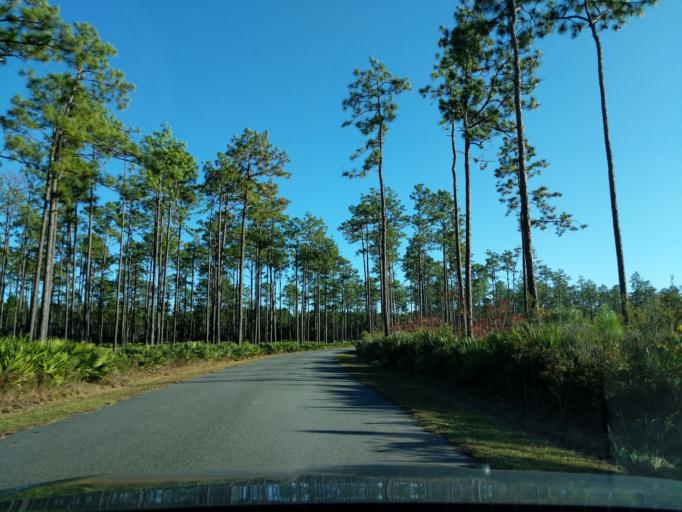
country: US
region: Georgia
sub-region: Charlton County
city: Folkston
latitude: 30.7224
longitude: -82.1398
